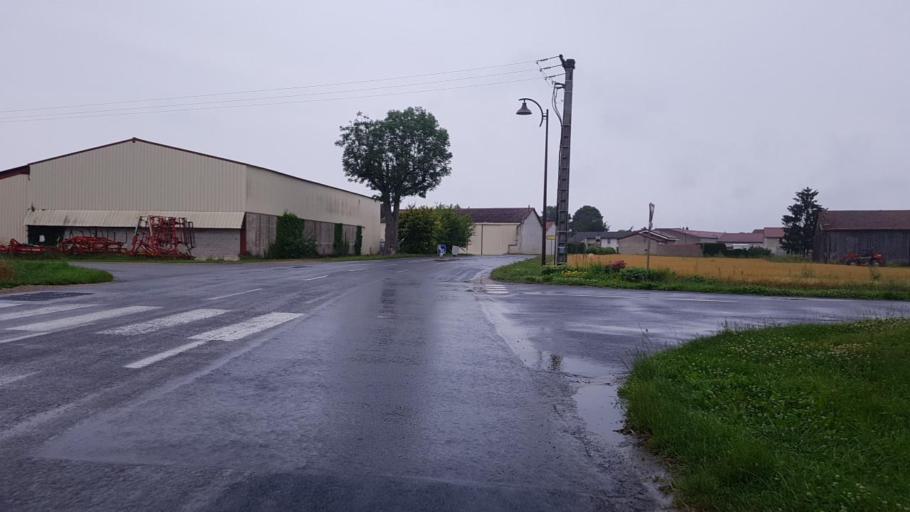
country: FR
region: Champagne-Ardenne
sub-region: Departement de la Marne
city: Sarry
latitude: 48.8798
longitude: 4.4505
